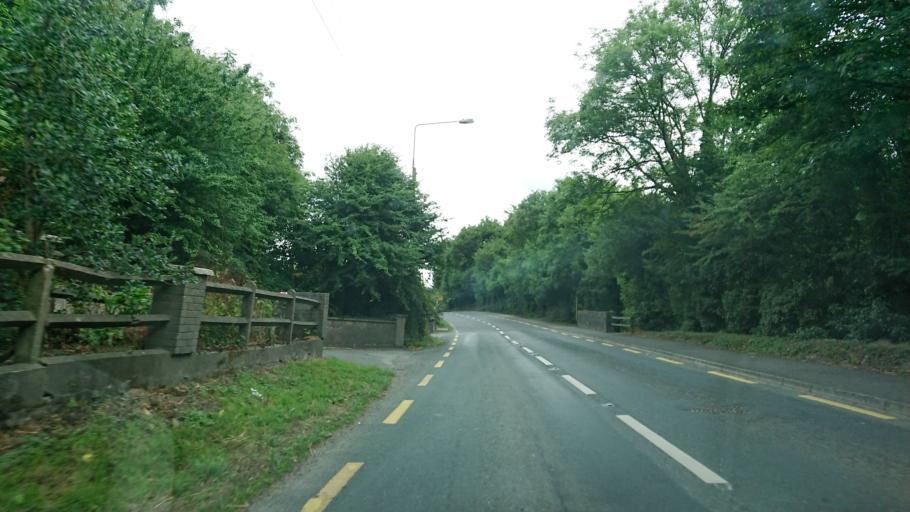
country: IE
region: Munster
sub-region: County Cork
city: Mallow
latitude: 52.1392
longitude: -8.6391
